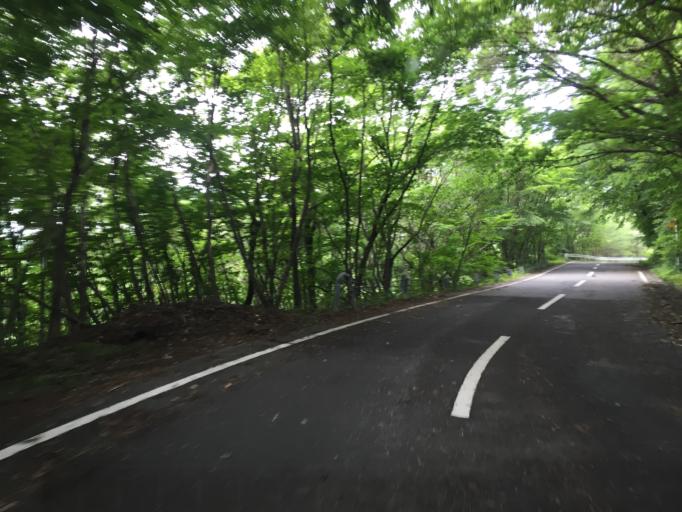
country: JP
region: Fukushima
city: Nihommatsu
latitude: 37.6614
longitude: 140.3294
